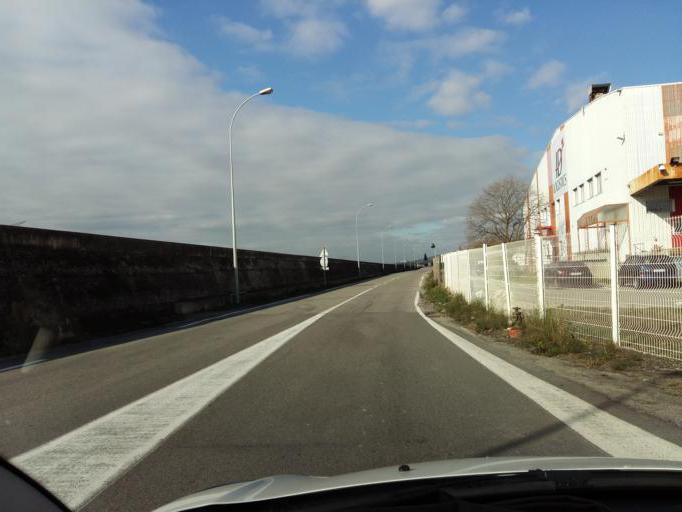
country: FR
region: Provence-Alpes-Cote d'Azur
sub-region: Departement du Vaucluse
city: Cavaillon
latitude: 43.8128
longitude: 5.0430
